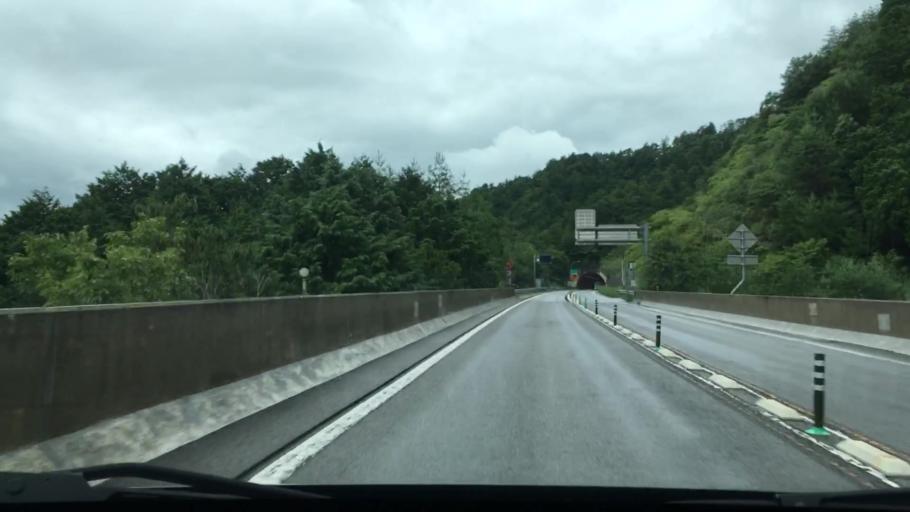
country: JP
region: Hyogo
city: Toyooka
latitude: 35.2773
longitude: 134.8162
